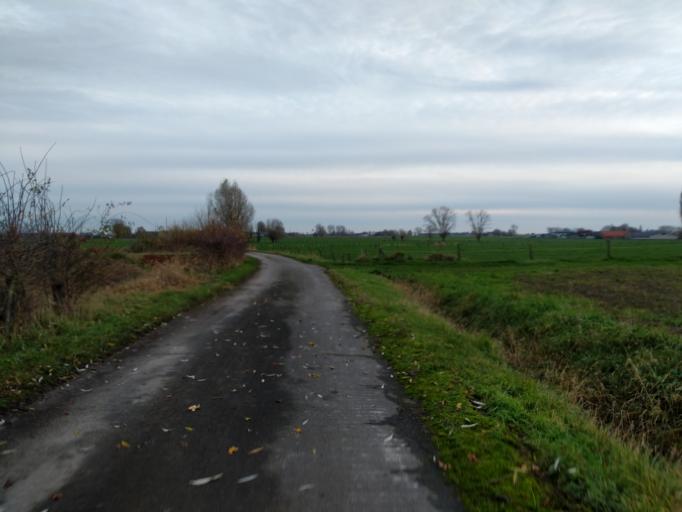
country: BE
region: Flanders
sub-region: Provincie West-Vlaanderen
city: Ruiselede
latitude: 51.0343
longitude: 3.4005
